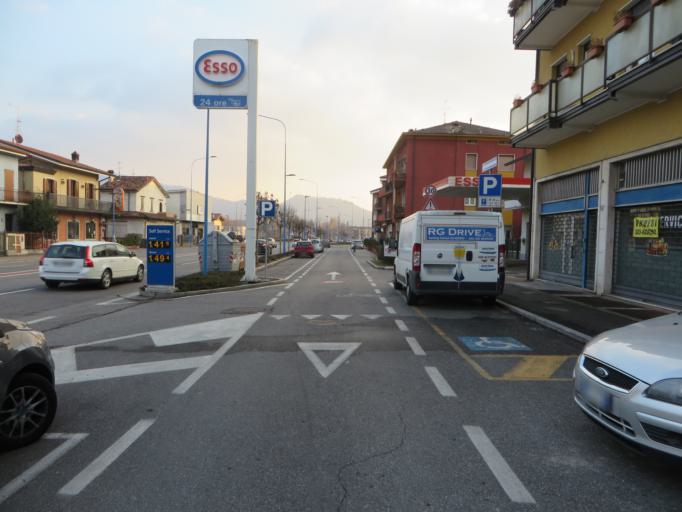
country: IT
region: Lombardy
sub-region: Provincia di Brescia
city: Bovezzo
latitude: 45.5741
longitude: 10.2309
